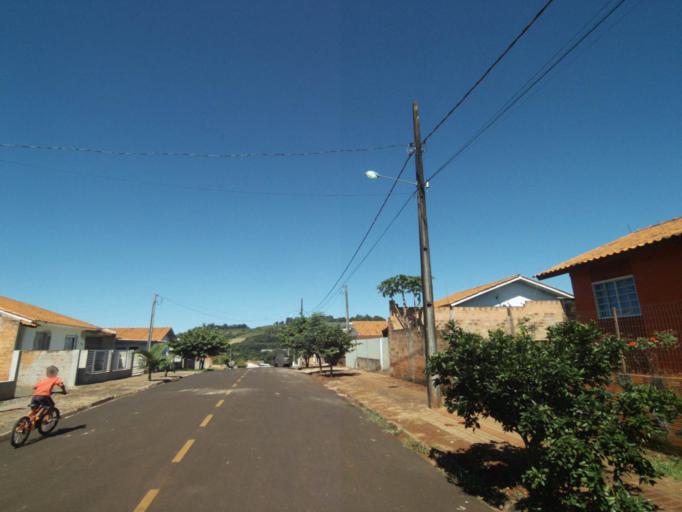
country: BR
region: Santa Catarina
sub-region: Sao Lourenco Do Oeste
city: Sao Lourenco dOeste
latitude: -26.2722
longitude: -52.7794
